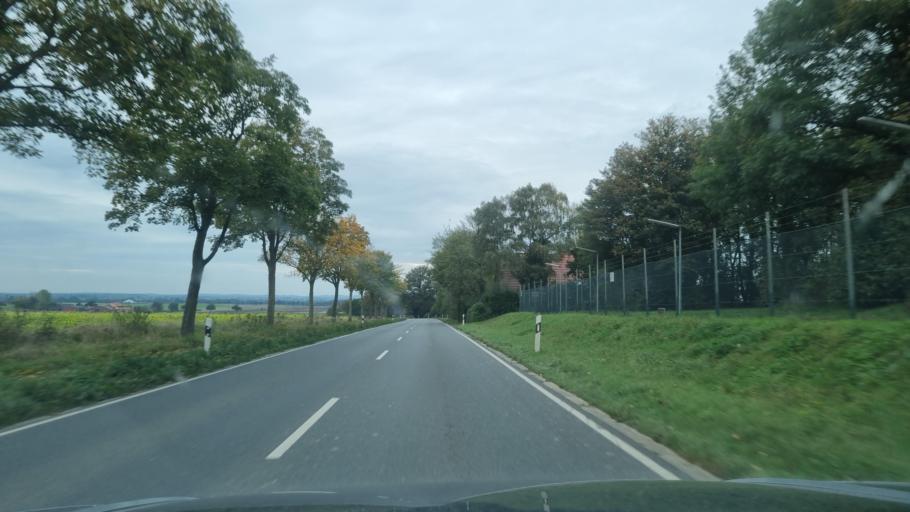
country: DE
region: North Rhine-Westphalia
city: Kalkar
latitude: 51.7203
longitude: 6.2984
